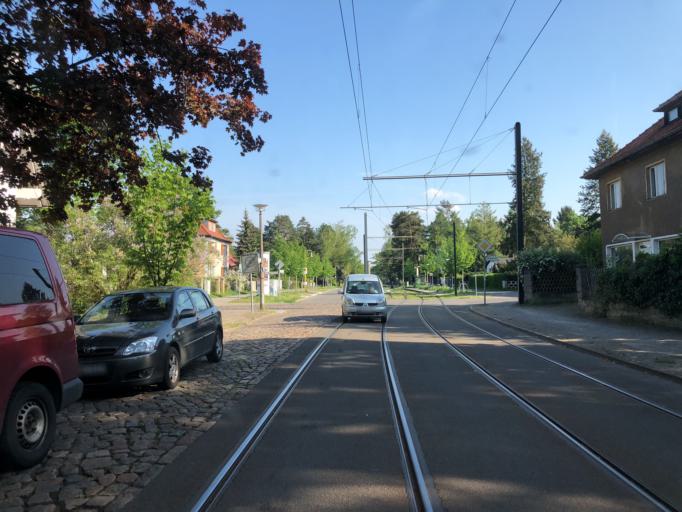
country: DE
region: Berlin
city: Schmockwitz
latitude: 52.3951
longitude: 13.6313
